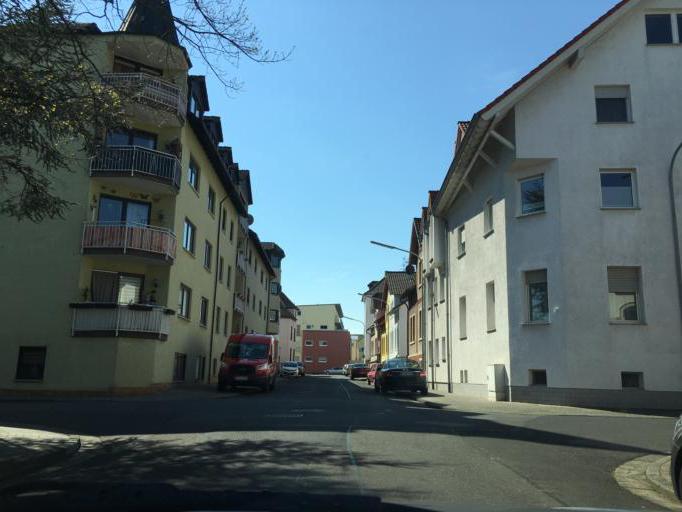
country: DE
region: Hesse
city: Obertshausen
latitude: 50.0740
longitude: 8.8487
